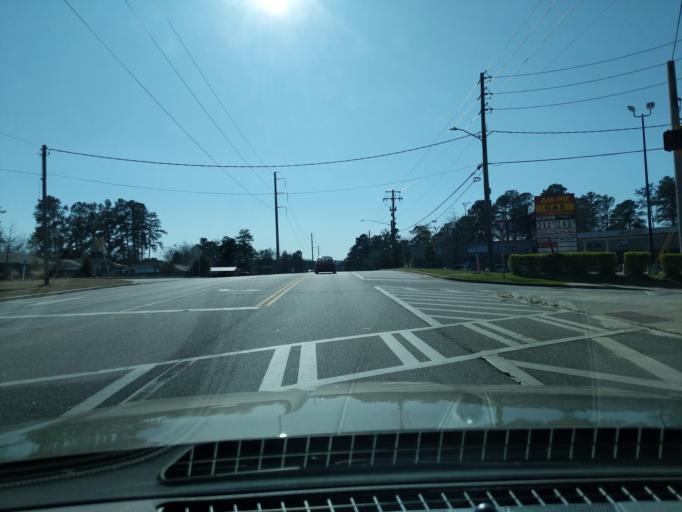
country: US
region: Georgia
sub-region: Columbia County
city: Grovetown
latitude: 33.4542
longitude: -82.2076
